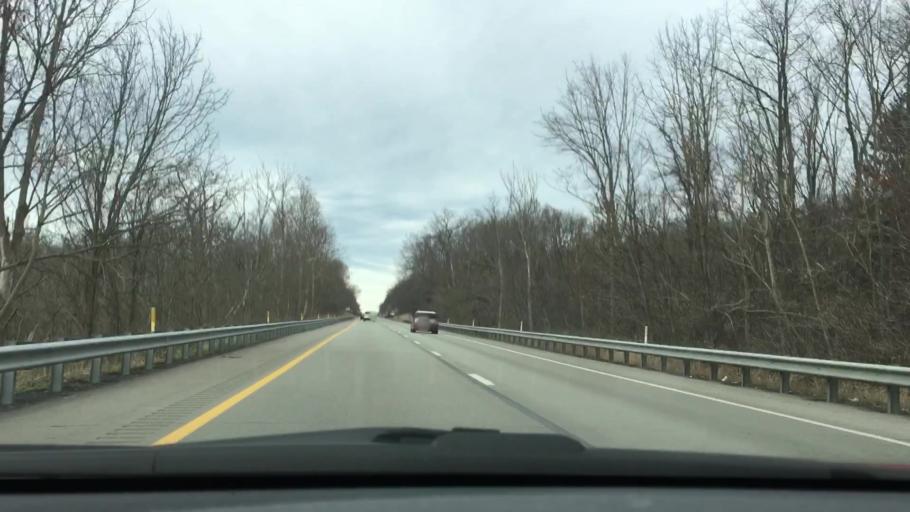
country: US
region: Pennsylvania
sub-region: Westmoreland County
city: Fellsburg
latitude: 40.1945
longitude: -79.8238
